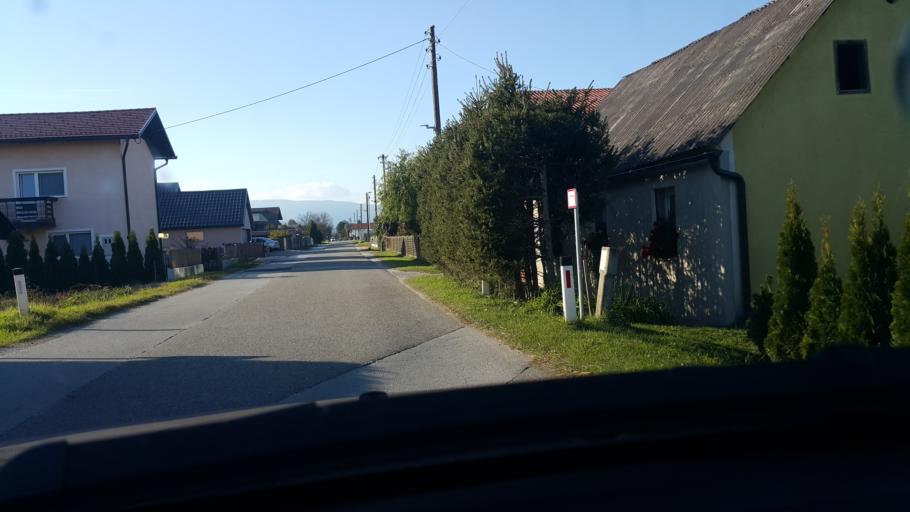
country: SI
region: Starse
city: Starse
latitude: 46.4361
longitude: 15.7319
